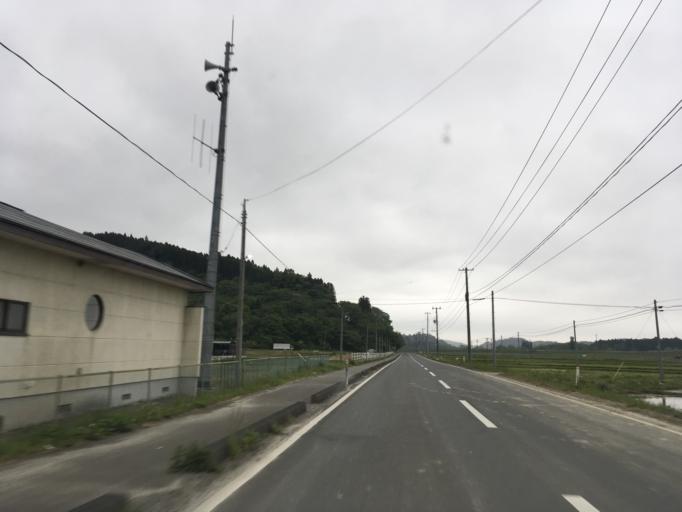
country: JP
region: Miyagi
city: Wakuya
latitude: 38.7265
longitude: 141.2969
